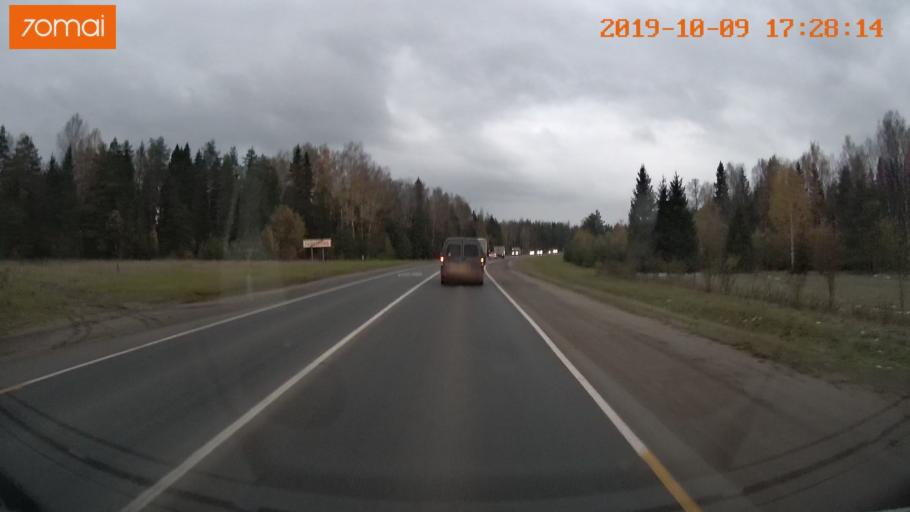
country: RU
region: Ivanovo
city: Furmanov
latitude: 57.1596
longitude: 41.0688
